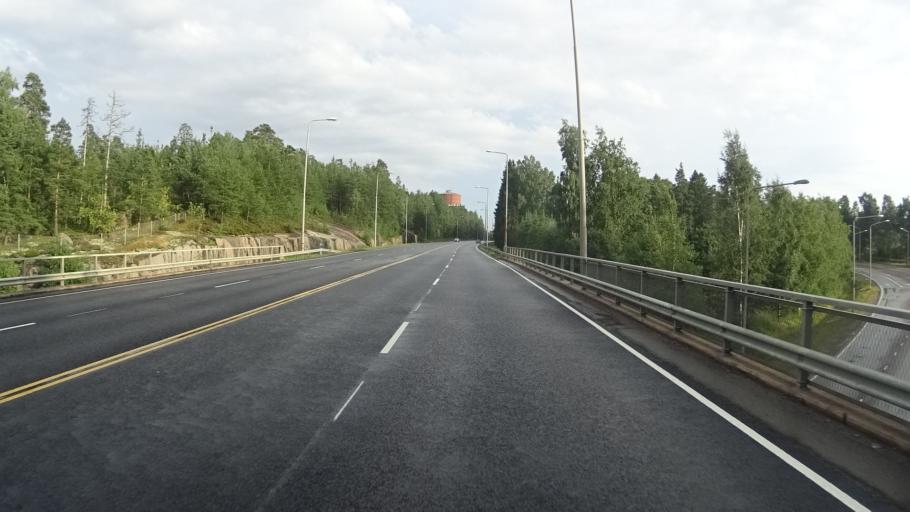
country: FI
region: Kymenlaakso
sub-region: Kotka-Hamina
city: Kotka
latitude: 60.4954
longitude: 26.8992
